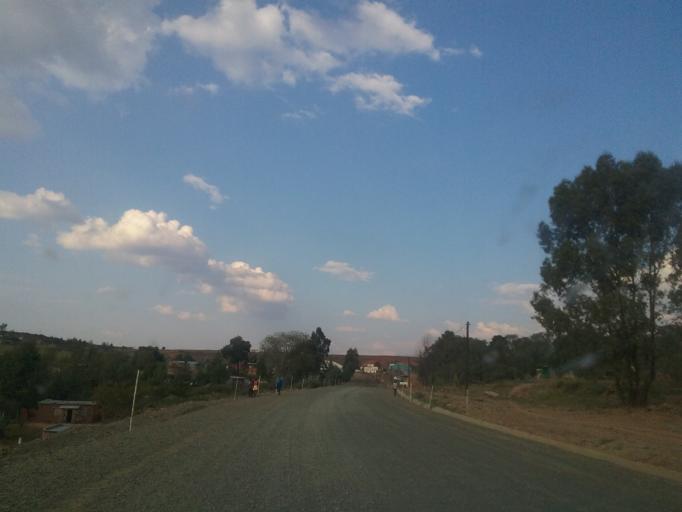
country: LS
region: Quthing
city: Quthing
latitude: -30.3947
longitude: 27.6207
